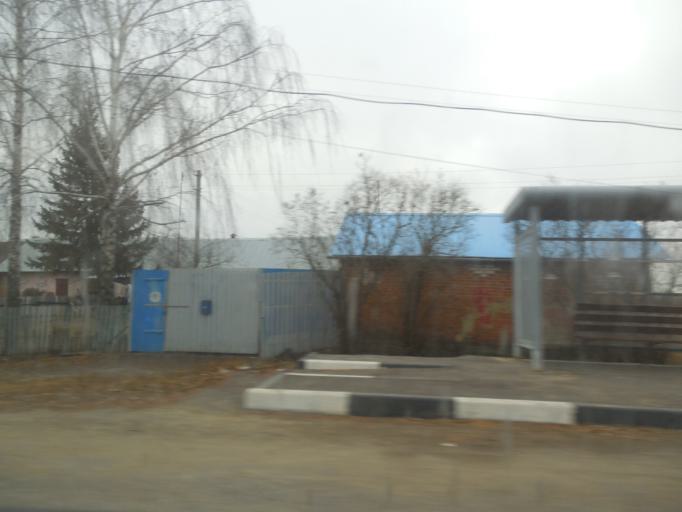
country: RU
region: Tula
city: Dubovka
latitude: 53.9002
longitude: 38.0367
